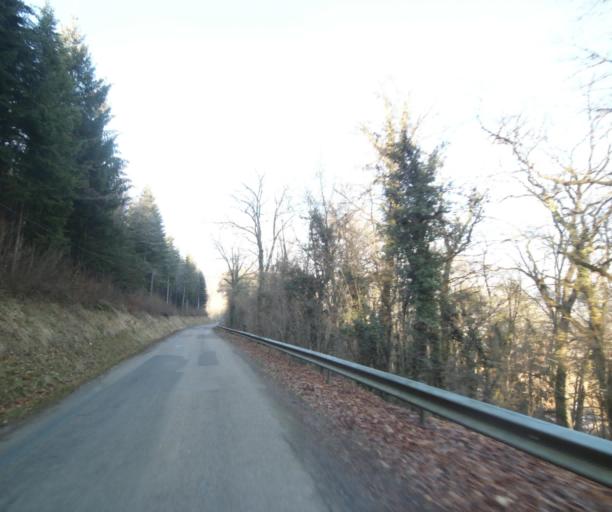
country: FR
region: Champagne-Ardenne
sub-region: Departement de la Haute-Marne
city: Chevillon
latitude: 48.5211
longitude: 5.0916
